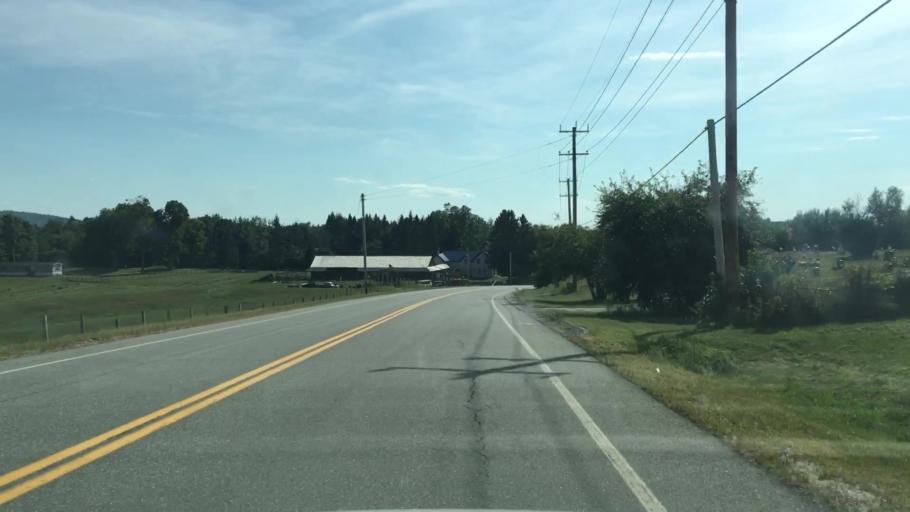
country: US
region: Maine
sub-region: Penobscot County
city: Lincoln
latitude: 45.3983
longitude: -68.5103
